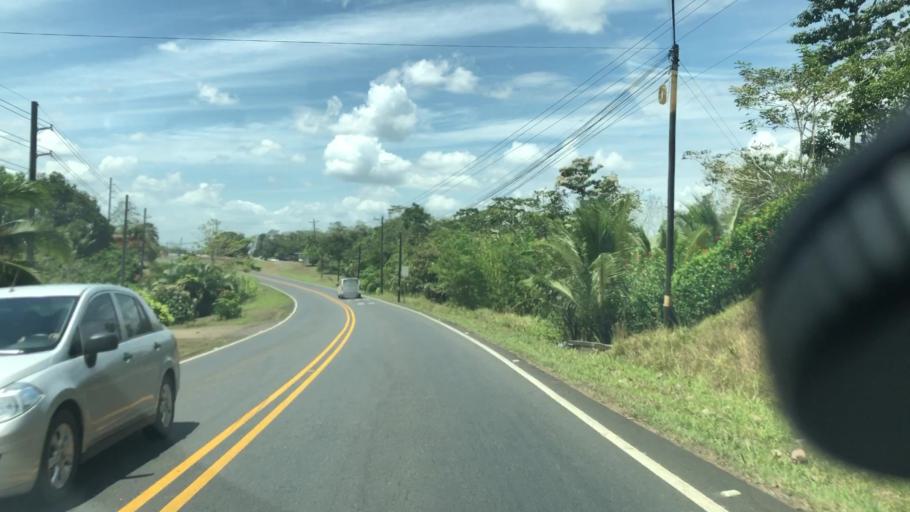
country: CR
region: Alajuela
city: Pital
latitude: 10.4579
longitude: -84.3886
